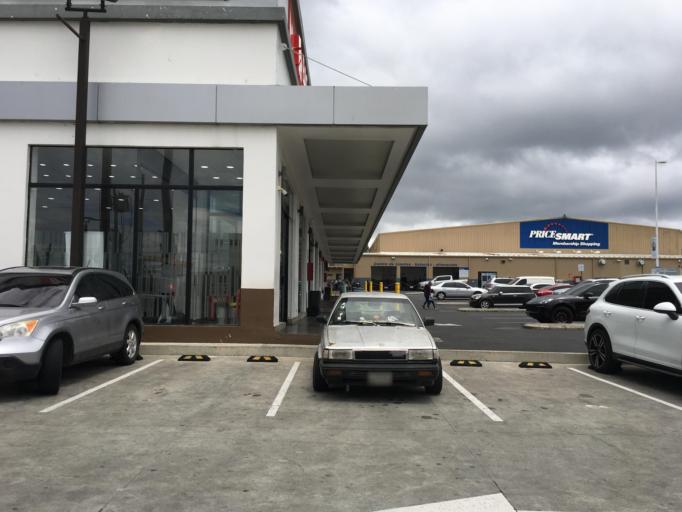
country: GT
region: Guatemala
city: Santa Catarina Pinula
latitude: 14.5145
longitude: -90.4755
